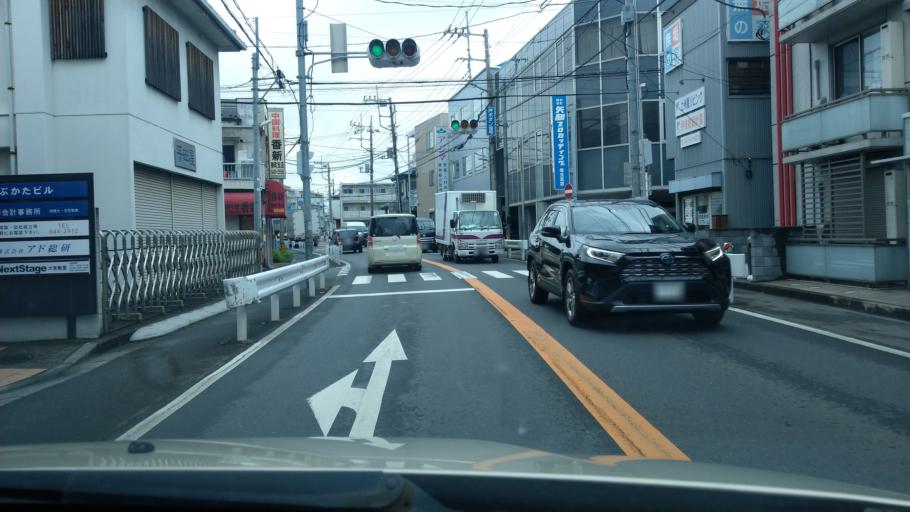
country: JP
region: Saitama
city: Saitama
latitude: 35.9096
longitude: 139.6341
